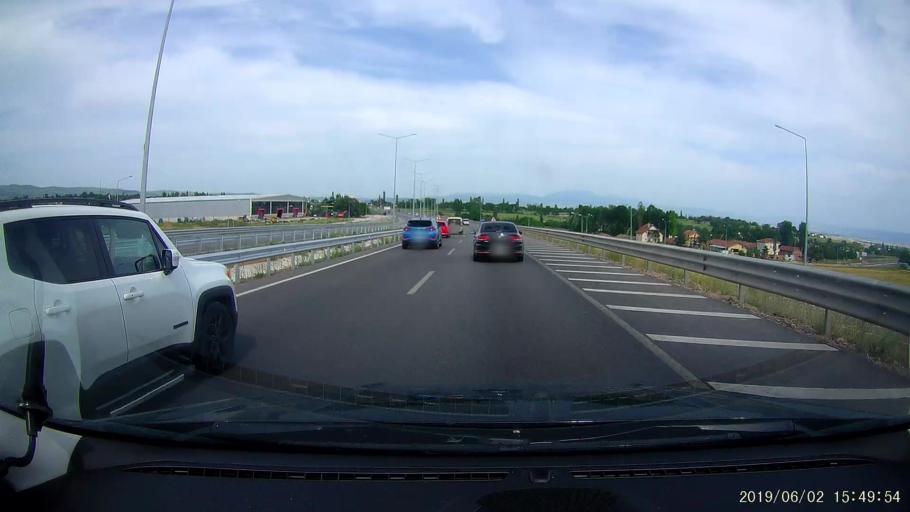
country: TR
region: Amasya
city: Merzifon
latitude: 40.8570
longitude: 35.4709
